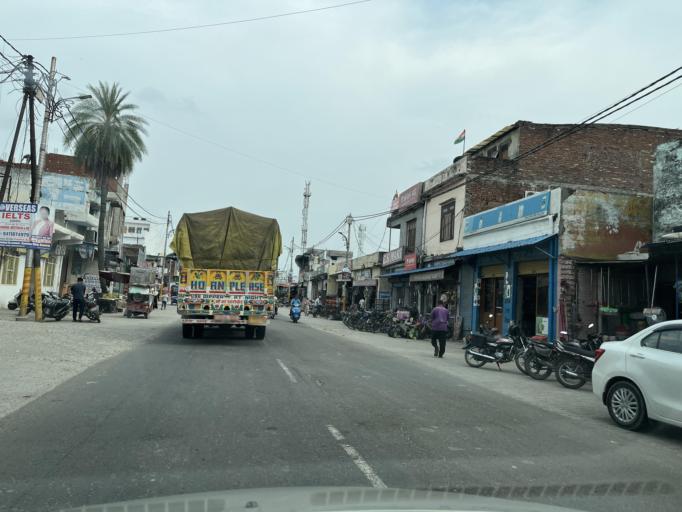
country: IN
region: Uttar Pradesh
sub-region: Rampur
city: Bilaspur
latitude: 29.0414
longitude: 79.2492
